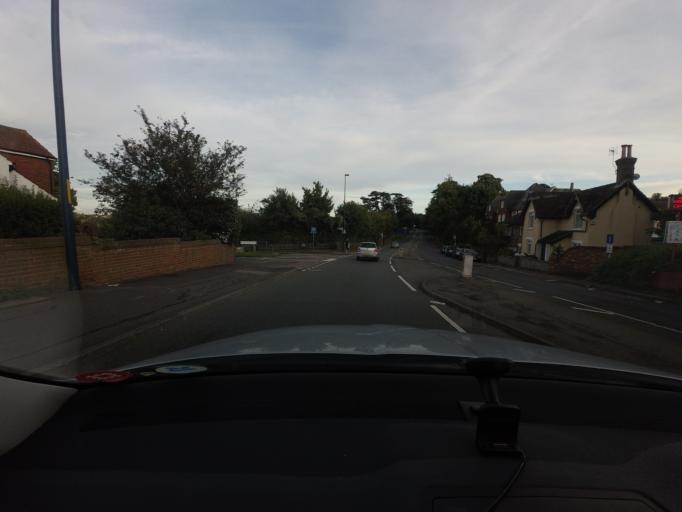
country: GB
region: England
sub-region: Kent
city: Maidstone
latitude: 51.2816
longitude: 0.5046
